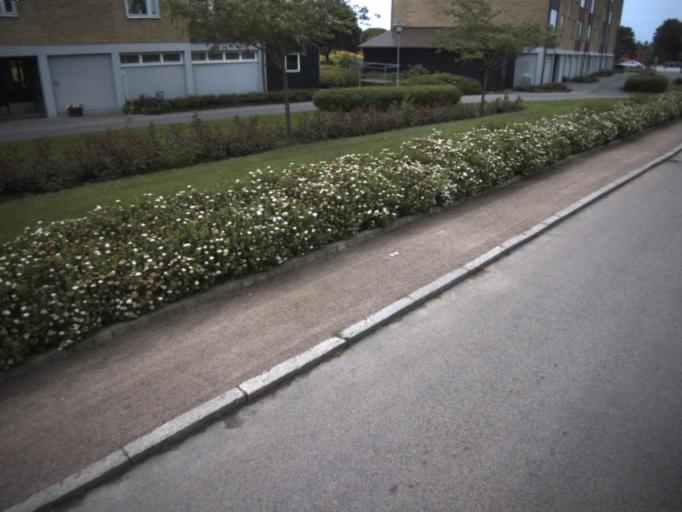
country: SE
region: Skane
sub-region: Helsingborg
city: Helsingborg
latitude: 56.0602
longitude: 12.7217
